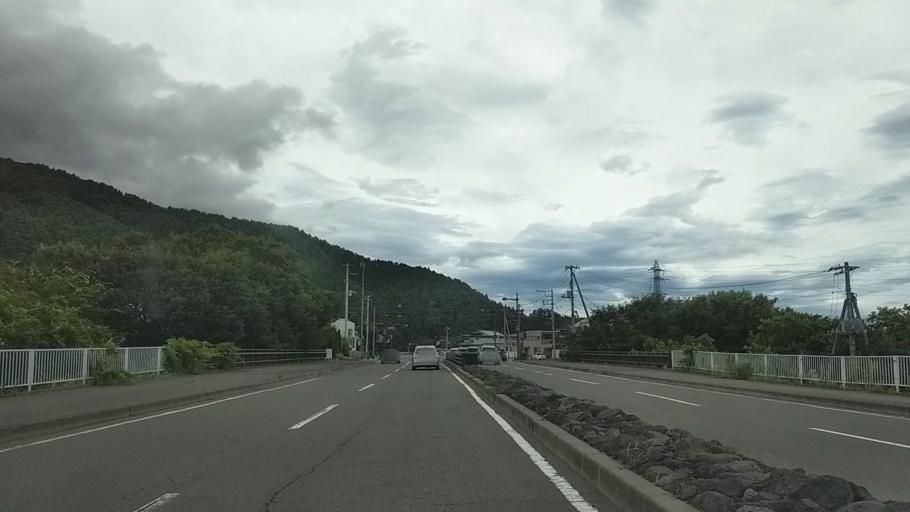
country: JP
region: Yamanashi
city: Fujikawaguchiko
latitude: 35.5005
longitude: 138.8180
